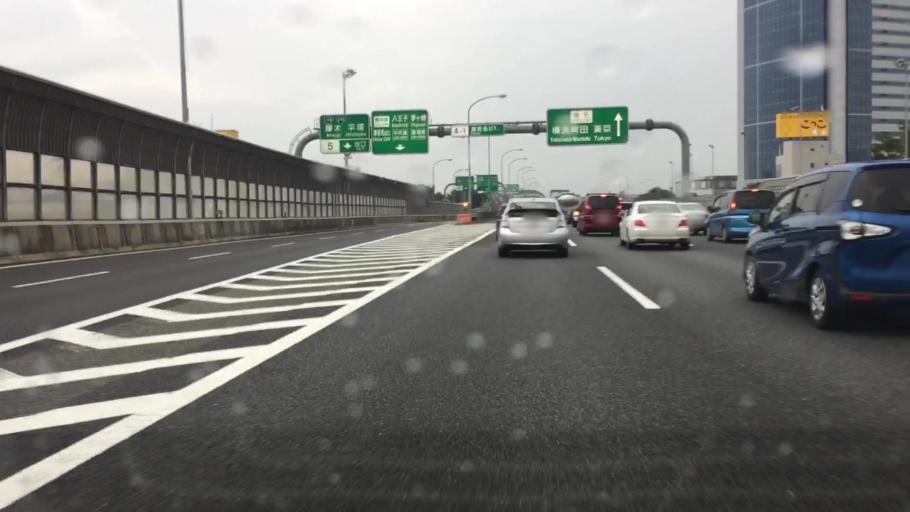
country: JP
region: Kanagawa
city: Atsugi
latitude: 35.4249
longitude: 139.3580
